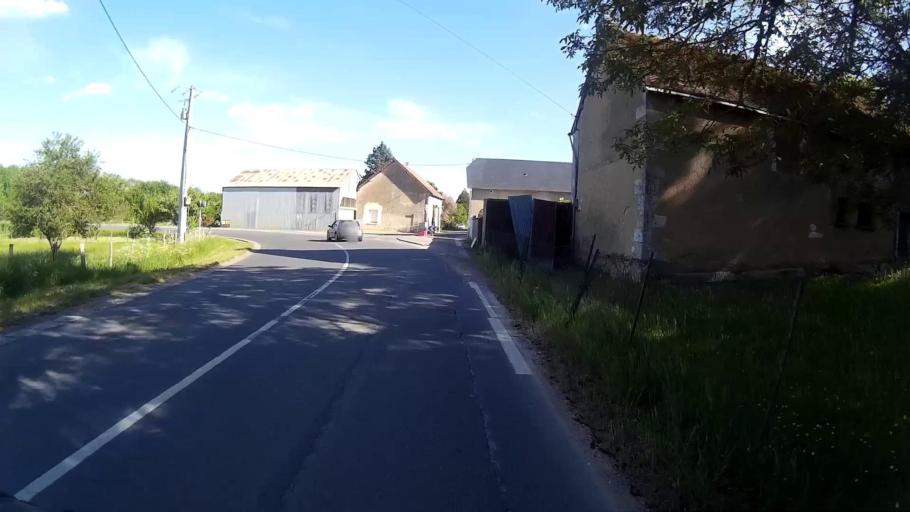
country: FR
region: Centre
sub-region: Departement du Loir-et-Cher
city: Villiers-sur-Loir
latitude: 47.8035
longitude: 0.9778
